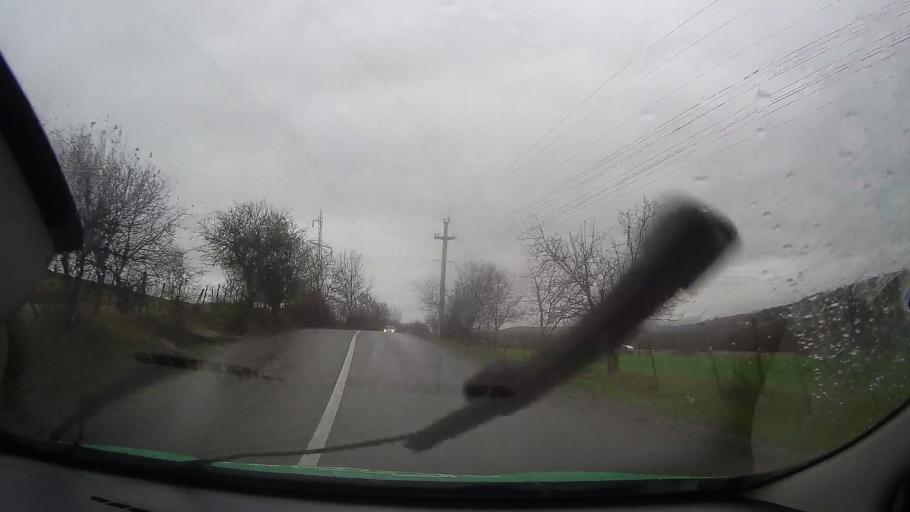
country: RO
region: Mures
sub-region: Comuna Brancovenesti
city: Valenii de Mures
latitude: 46.9220
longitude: 24.7748
